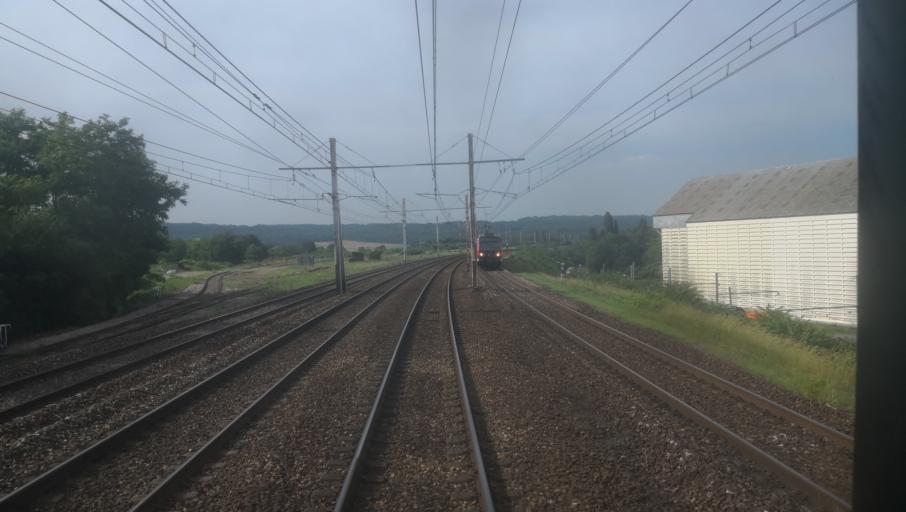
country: FR
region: Ile-de-France
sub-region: Departement de l'Essonne
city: Morigny-Champigny
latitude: 48.4525
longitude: 2.1679
